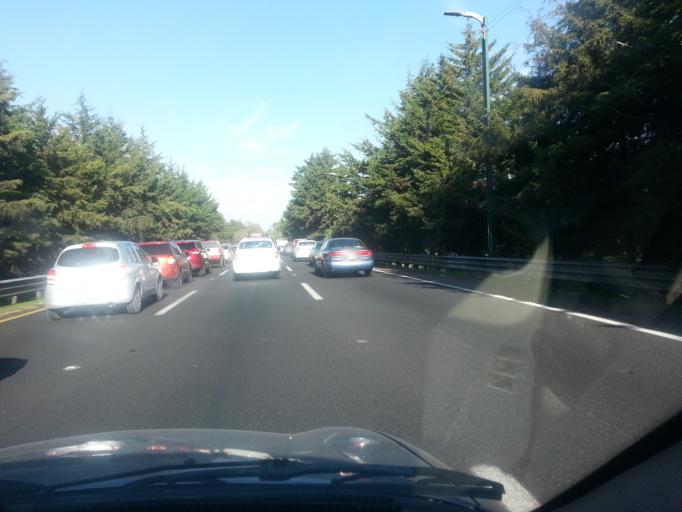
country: MX
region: Mexico
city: Santa Maria Totoltepec
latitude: 19.2875
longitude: -99.5953
